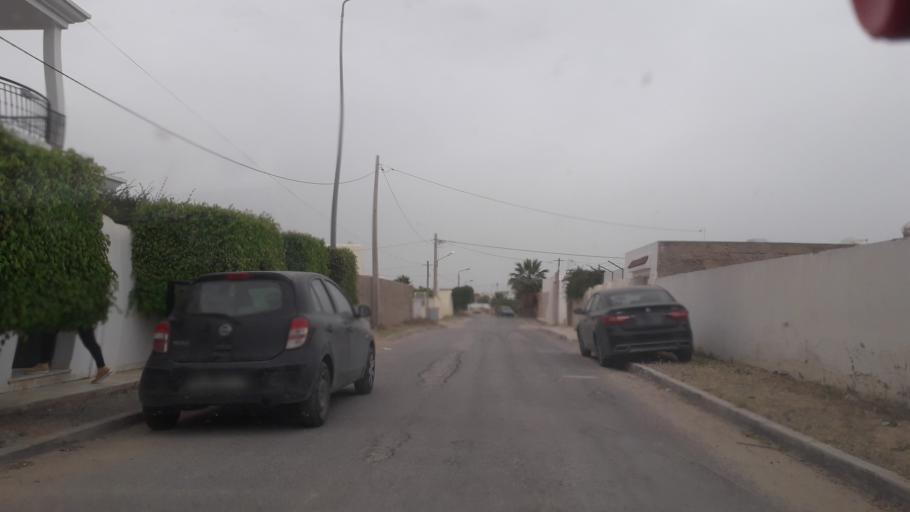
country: TN
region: Safaqis
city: Al Qarmadah
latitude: 34.7888
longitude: 10.7648
